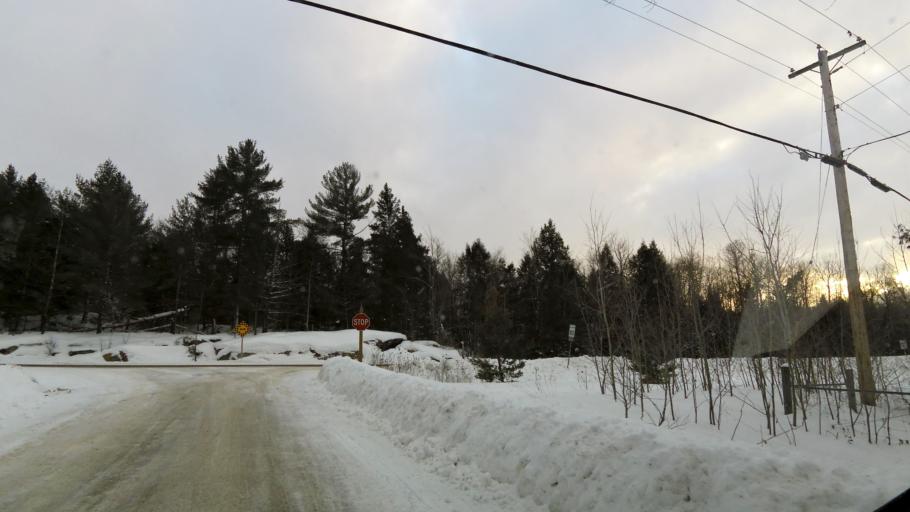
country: CA
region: Ontario
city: Omemee
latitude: 44.7253
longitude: -78.8186
